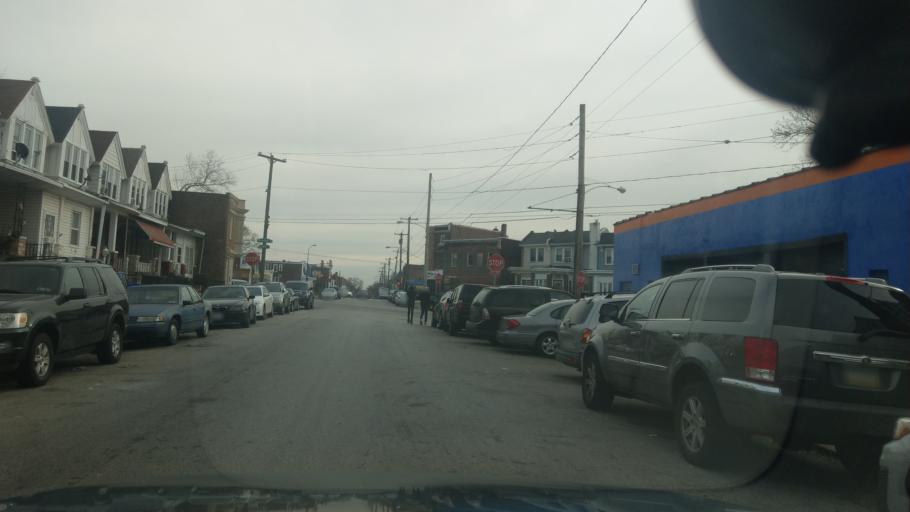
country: US
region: Pennsylvania
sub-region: Montgomery County
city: Wyncote
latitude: 40.0490
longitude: -75.1520
